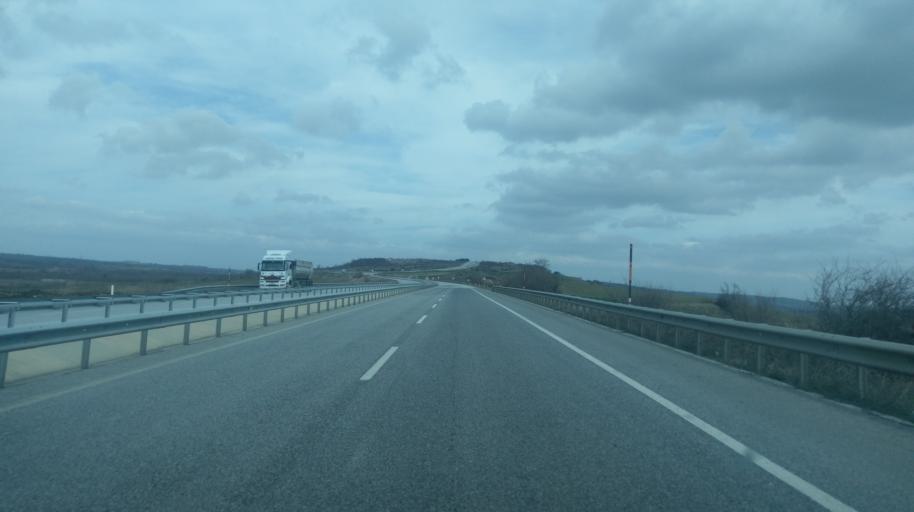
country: TR
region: Edirne
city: Uzun Keupru
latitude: 41.3071
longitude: 26.7128
